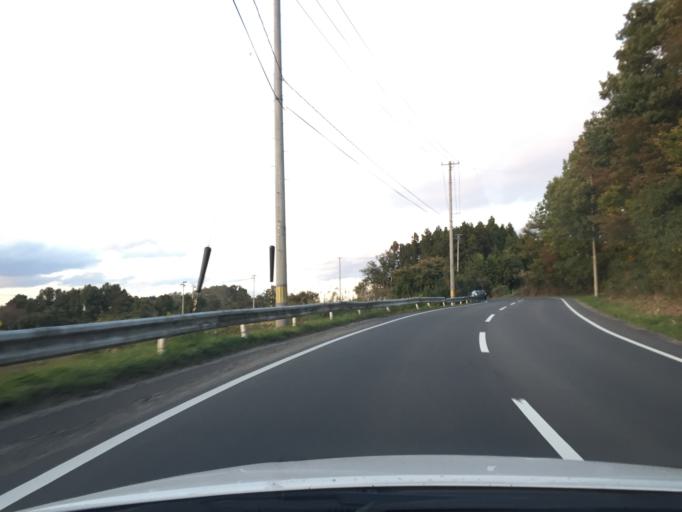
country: JP
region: Fukushima
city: Miharu
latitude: 37.3953
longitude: 140.4424
